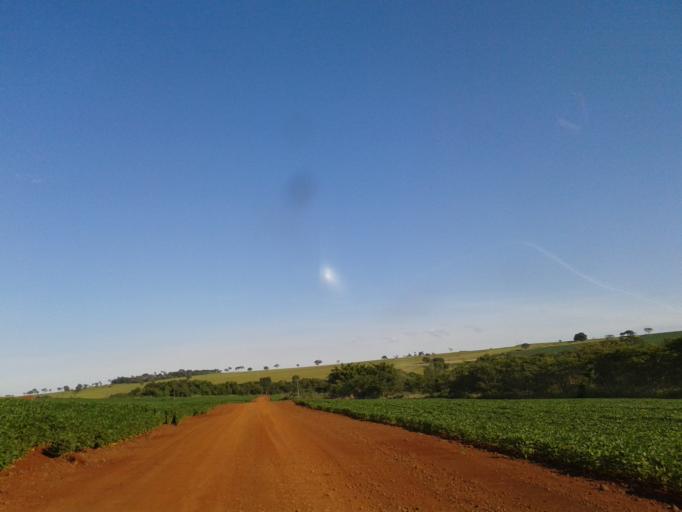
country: BR
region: Minas Gerais
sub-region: Centralina
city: Centralina
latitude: -18.6911
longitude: -49.2799
